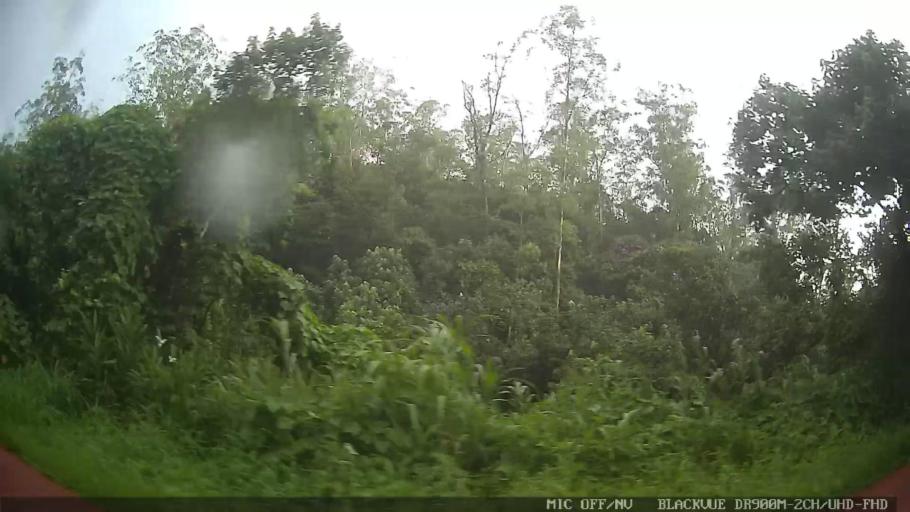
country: BR
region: Sao Paulo
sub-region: Ribeirao Pires
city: Ribeirao Pires
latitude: -23.6994
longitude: -46.3859
